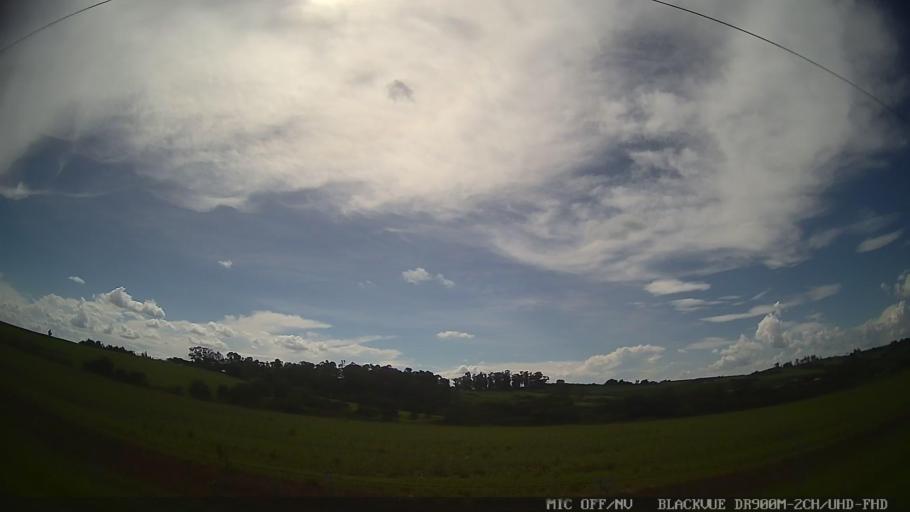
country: BR
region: Sao Paulo
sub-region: Conchas
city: Conchas
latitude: -22.9656
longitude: -47.9833
